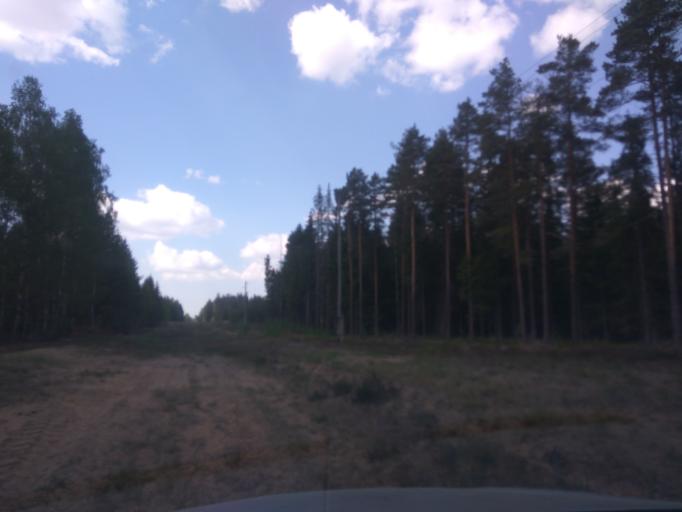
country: LV
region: Kuldigas Rajons
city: Kuldiga
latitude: 57.1834
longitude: 21.9971
